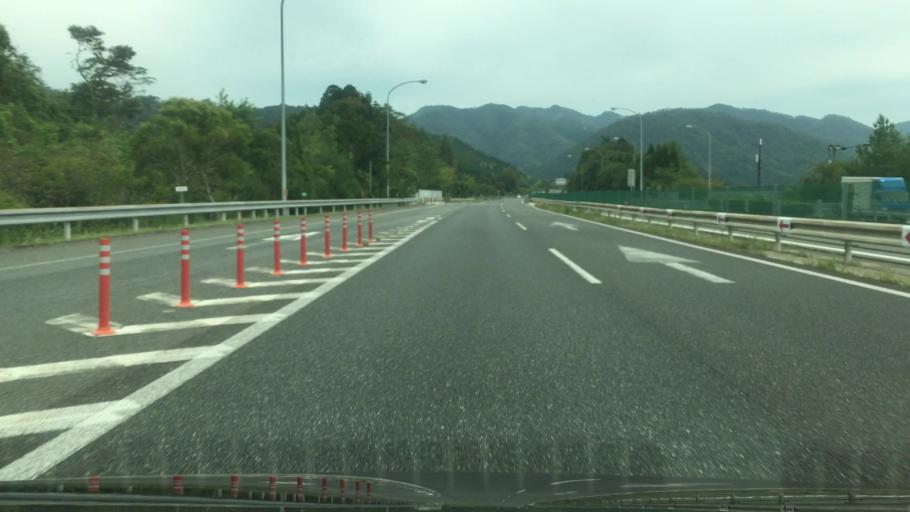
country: JP
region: Hyogo
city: Sasayama
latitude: 35.0935
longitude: 135.1678
